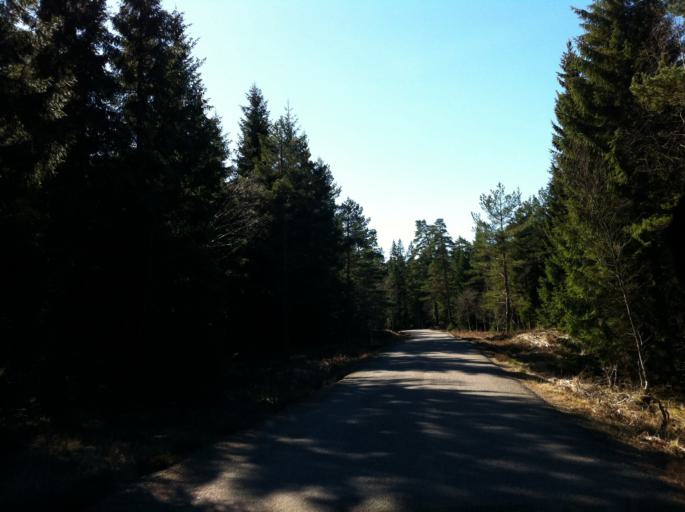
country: SE
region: Vaestra Goetaland
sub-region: Vanersborgs Kommun
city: Vargon
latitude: 58.3770
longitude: 12.4381
